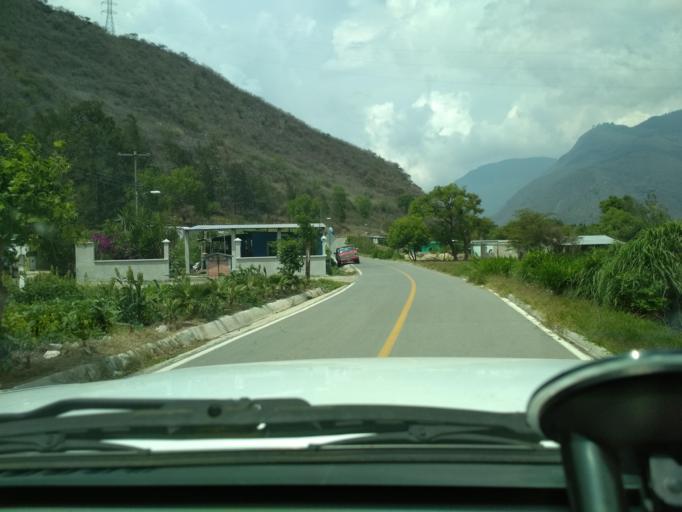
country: MX
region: Veracruz
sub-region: Nogales
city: Taza de Agua Ojo Zarco
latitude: 18.7820
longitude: -97.2157
